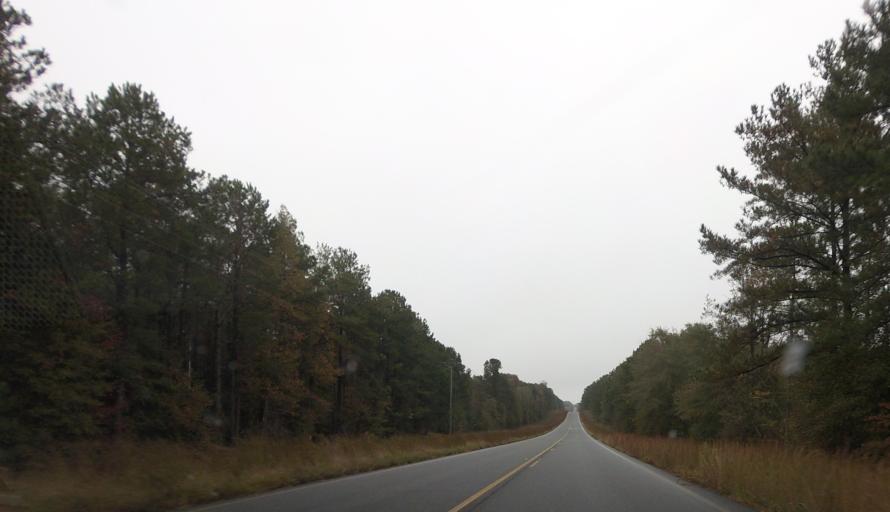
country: US
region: Georgia
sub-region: Marion County
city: Buena Vista
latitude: 32.3945
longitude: -84.4242
